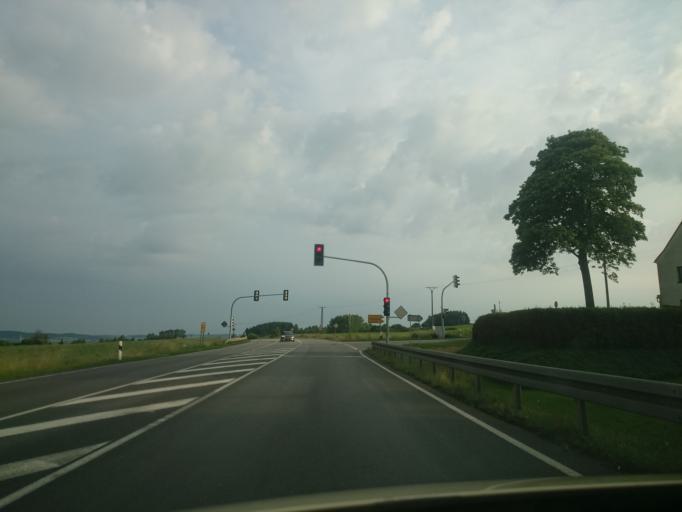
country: DE
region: Saxony
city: Grossolbersdorf
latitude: 50.7195
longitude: 13.0988
